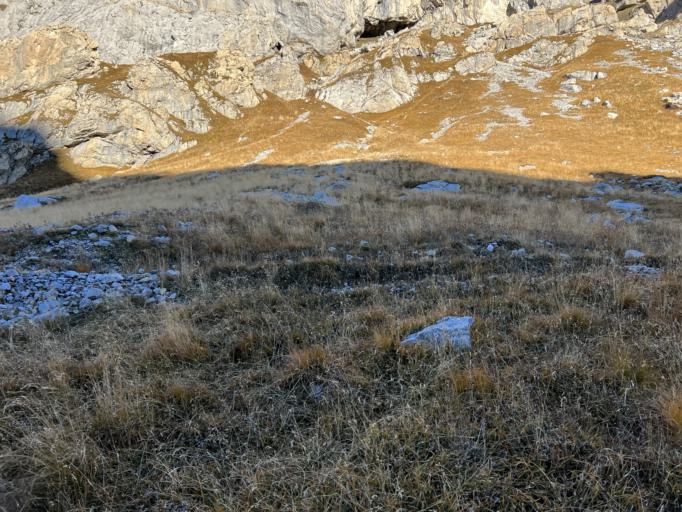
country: IT
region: Friuli Venezia Giulia
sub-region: Provincia di Udine
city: Forni Avoltri
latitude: 46.6276
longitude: 12.7267
